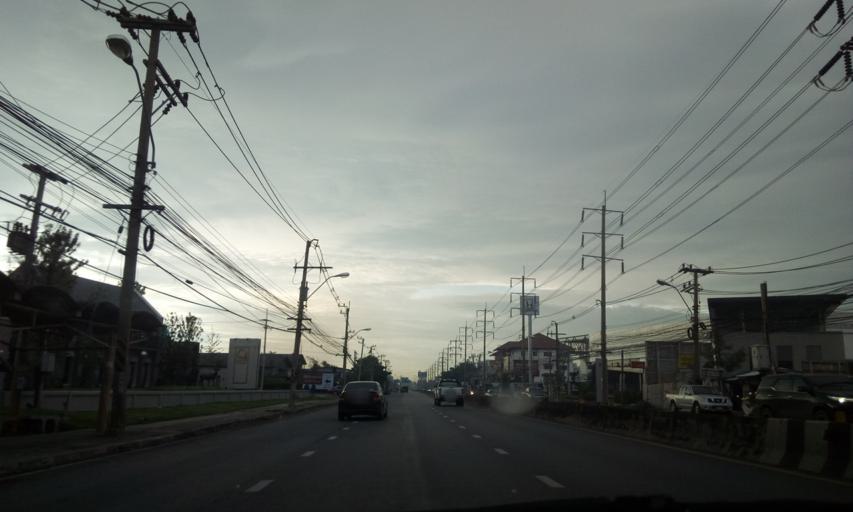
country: TH
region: Phra Nakhon Si Ayutthaya
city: Ban Bang Kadi Pathum Thani
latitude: 13.9579
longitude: 100.5506
